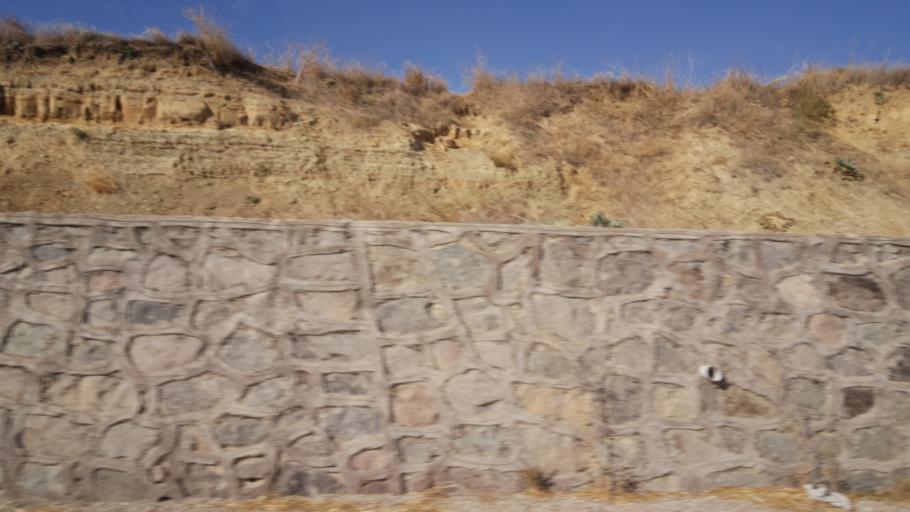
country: TR
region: Ankara
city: Yenice
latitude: 39.3655
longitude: 32.6874
